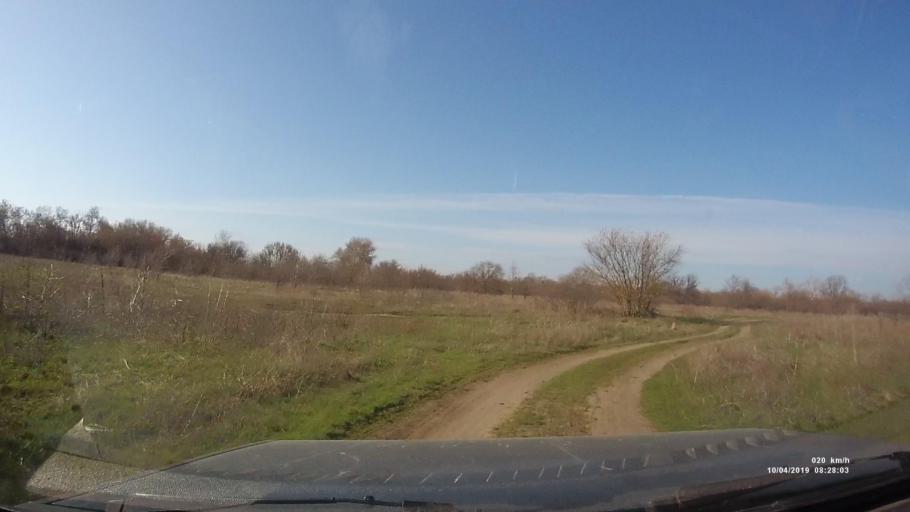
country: RU
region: Rostov
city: Kamensk-Shakhtinskiy
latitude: 48.3575
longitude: 40.2236
